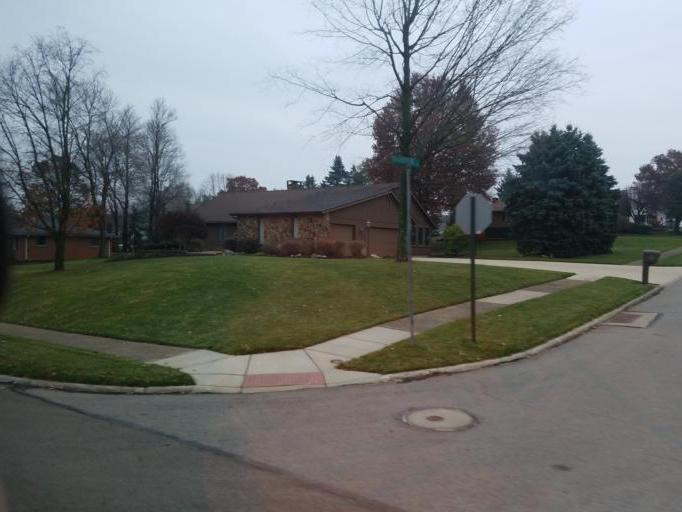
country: US
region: Ohio
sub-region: Richland County
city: Lexington
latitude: 40.6982
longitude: -82.5395
